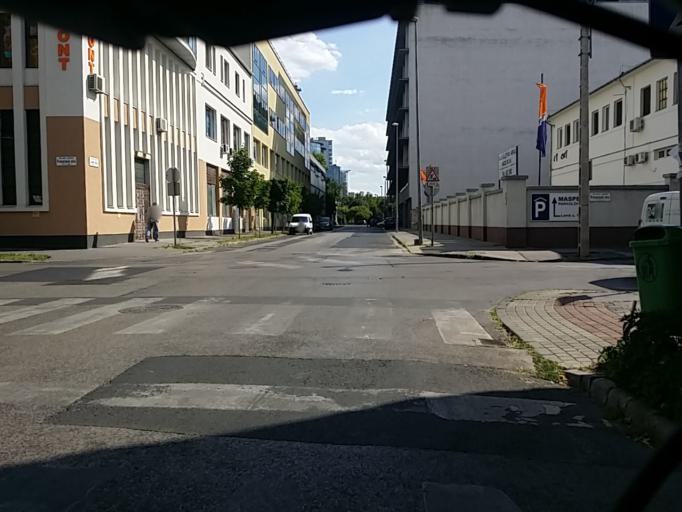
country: HU
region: Budapest
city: Budapest XIII. keruelet
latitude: 47.5364
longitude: 19.0706
